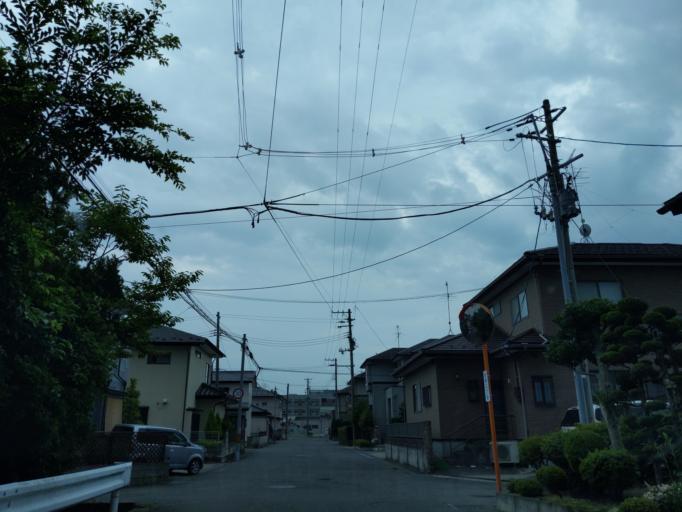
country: JP
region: Fukushima
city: Koriyama
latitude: 37.3890
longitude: 140.3487
